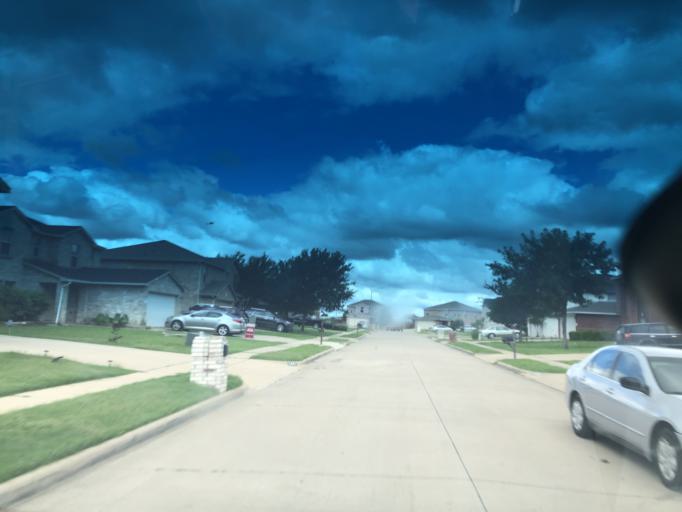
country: US
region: Texas
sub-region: Dallas County
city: Grand Prairie
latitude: 32.7057
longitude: -97.0406
